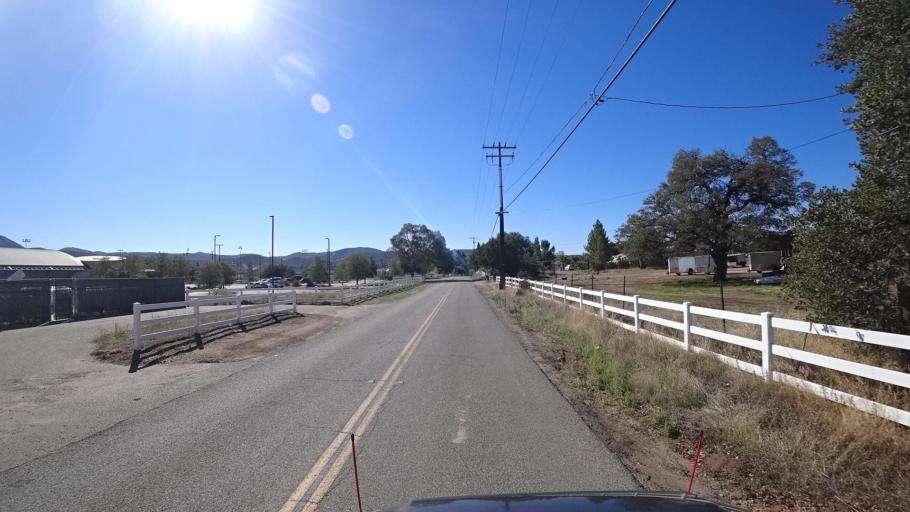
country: US
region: California
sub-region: San Diego County
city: Alpine
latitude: 32.8581
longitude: -116.6982
